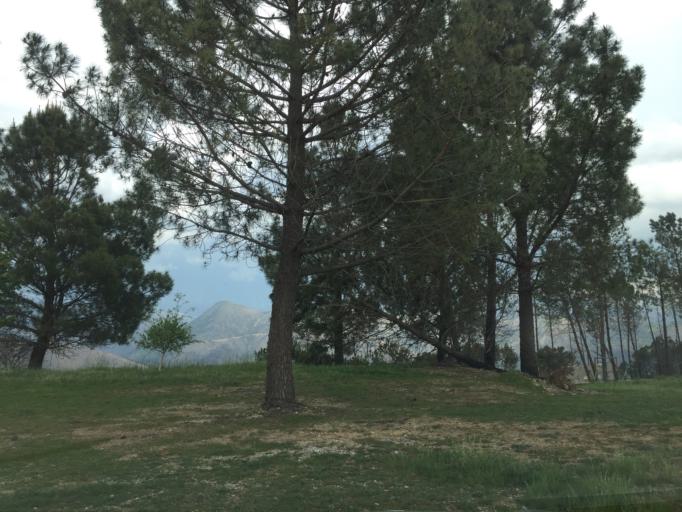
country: PT
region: Coimbra
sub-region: Arganil
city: Arganil
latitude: 40.1630
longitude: -7.9777
